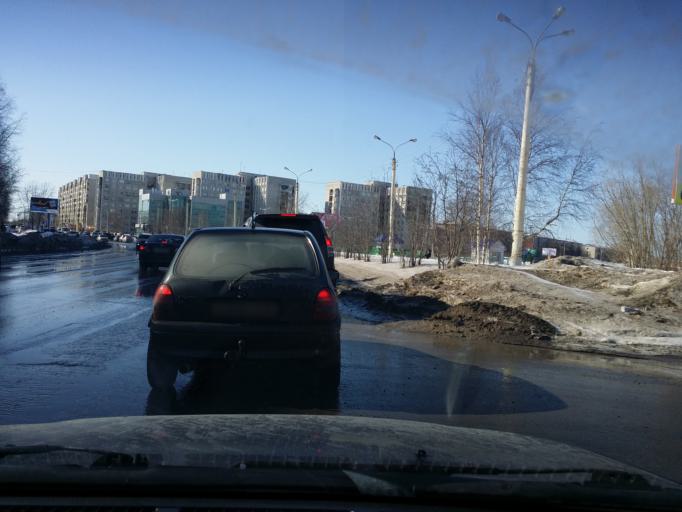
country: RU
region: Khanty-Mansiyskiy Avtonomnyy Okrug
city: Nizhnevartovsk
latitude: 60.9453
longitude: 76.5699
